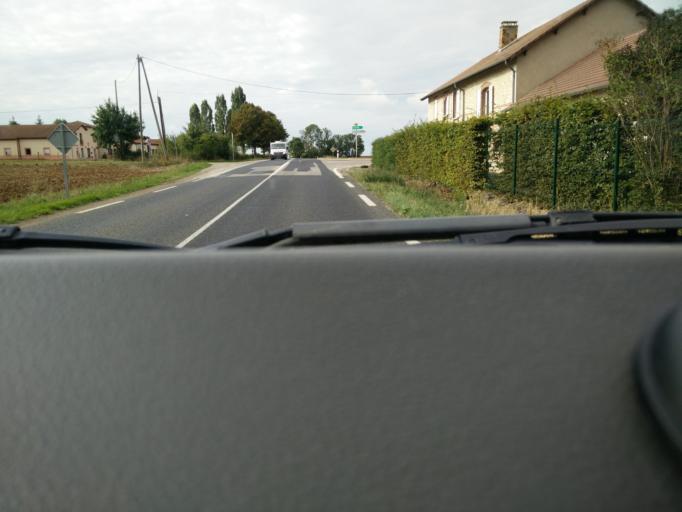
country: FR
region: Lorraine
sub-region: Departement de Meurthe-et-Moselle
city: Montauville
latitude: 48.8947
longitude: 5.9788
